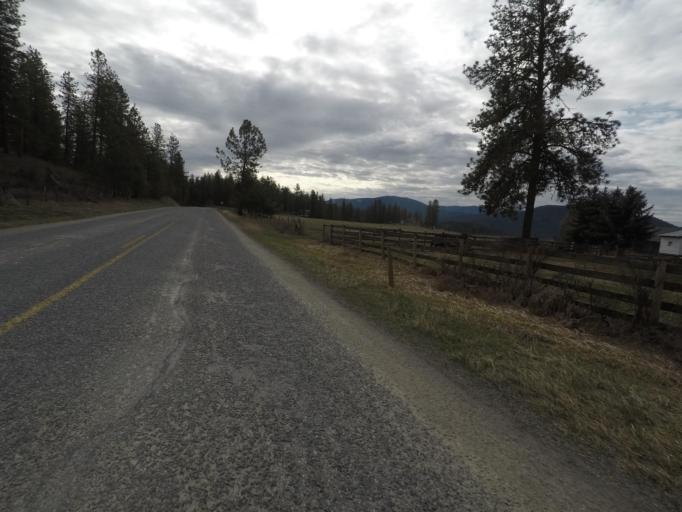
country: US
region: Washington
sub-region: Stevens County
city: Colville
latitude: 48.4988
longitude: -117.8411
